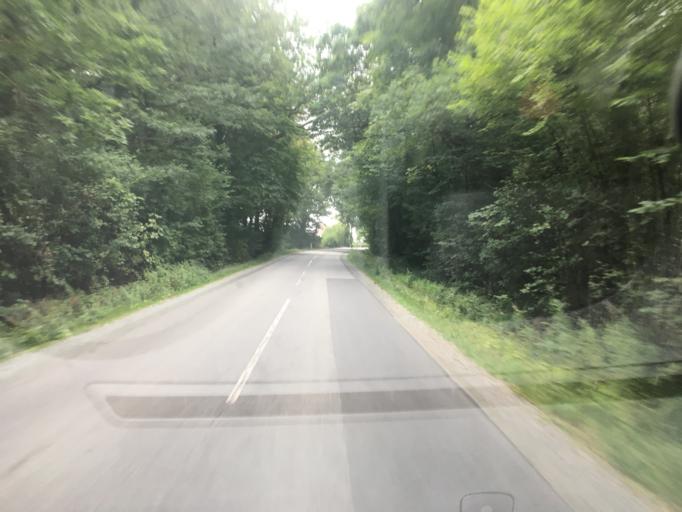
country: DK
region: South Denmark
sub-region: Tonder Kommune
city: Logumkloster
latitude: 55.0095
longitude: 8.9676
